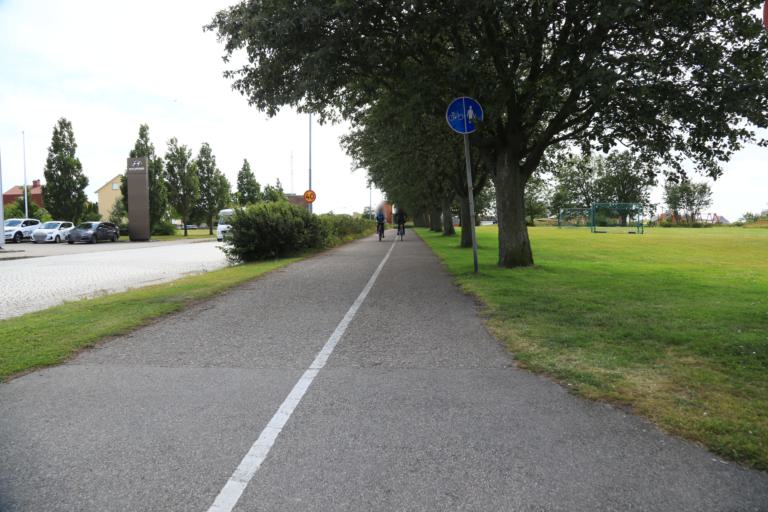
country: SE
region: Halland
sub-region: Varbergs Kommun
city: Varberg
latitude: 57.1134
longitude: 12.2553
